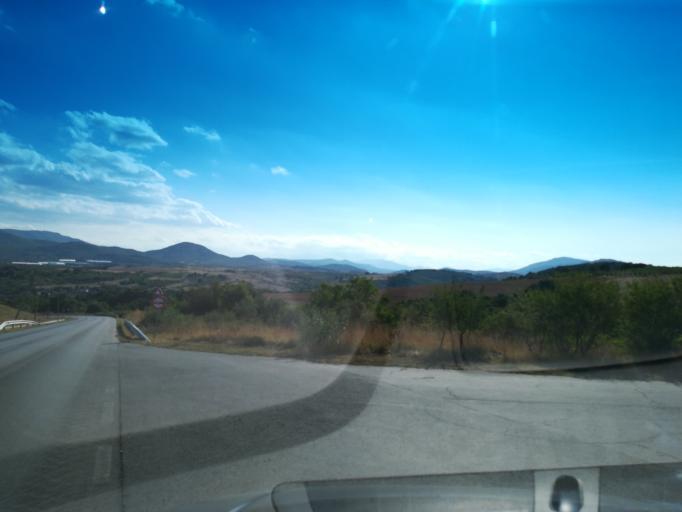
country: BG
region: Khaskovo
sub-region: Obshtina Mineralni Bani
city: Mineralni Bani
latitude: 41.9711
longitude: 25.3503
